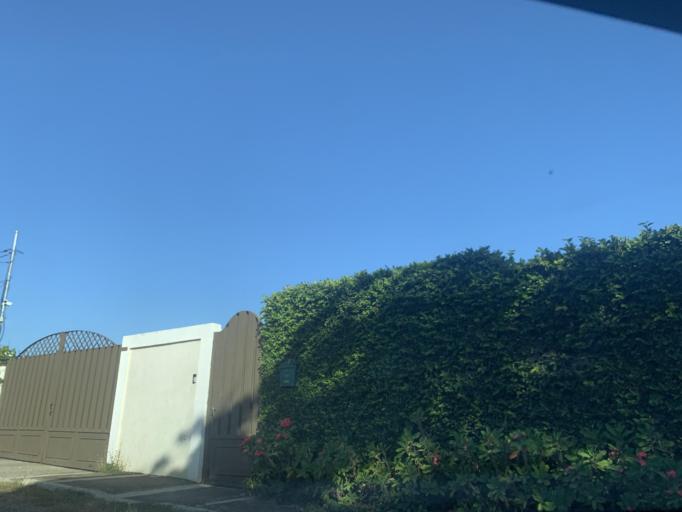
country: DO
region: Puerto Plata
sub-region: Puerto Plata
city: Puerto Plata
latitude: 19.8105
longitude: -70.7142
